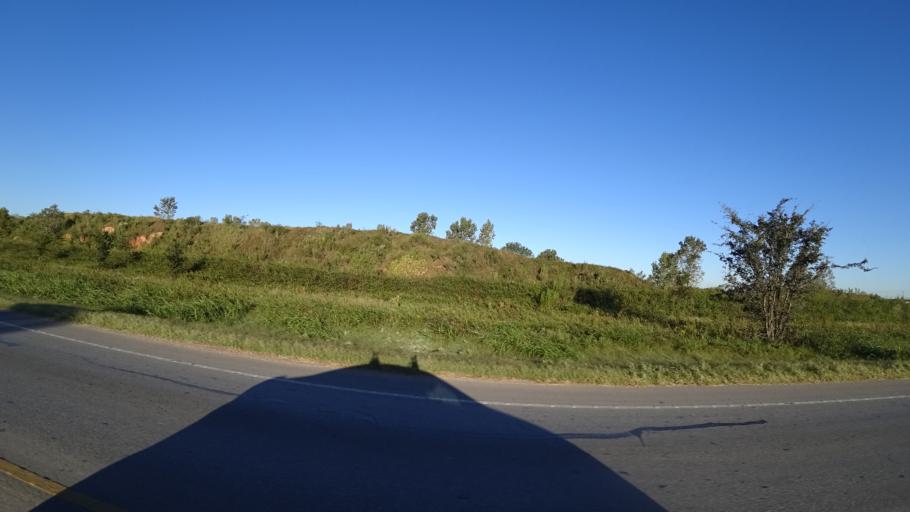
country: US
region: Texas
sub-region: Travis County
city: Hornsby Bend
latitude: 30.2307
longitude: -97.6284
